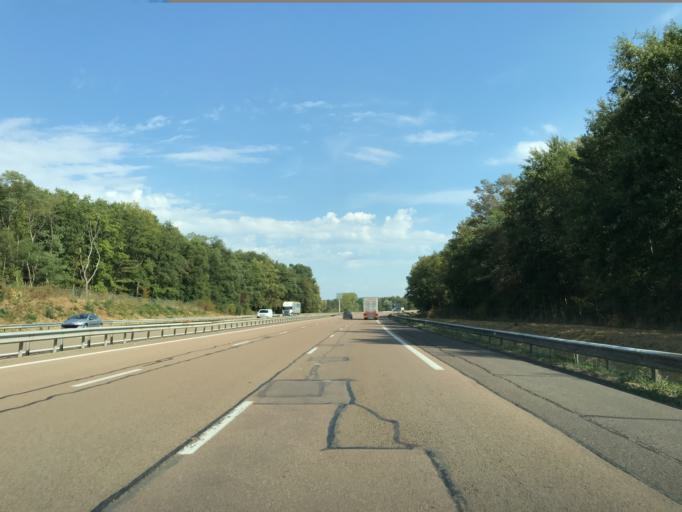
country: FR
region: Bourgogne
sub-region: Departement de l'Yonne
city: Appoigny
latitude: 47.8645
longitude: 3.5156
